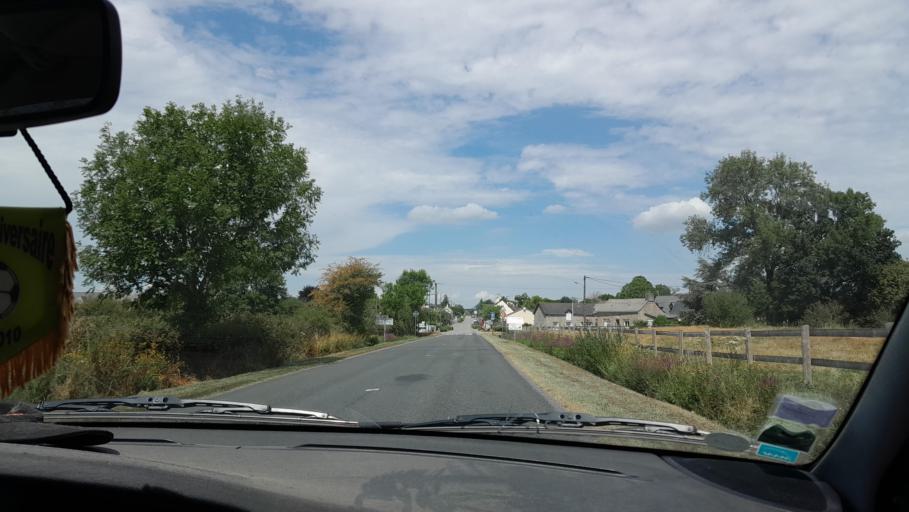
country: FR
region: Pays de la Loire
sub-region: Departement de la Mayenne
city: Saint-Pierre-la-Cour
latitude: 48.1037
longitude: -1.0211
